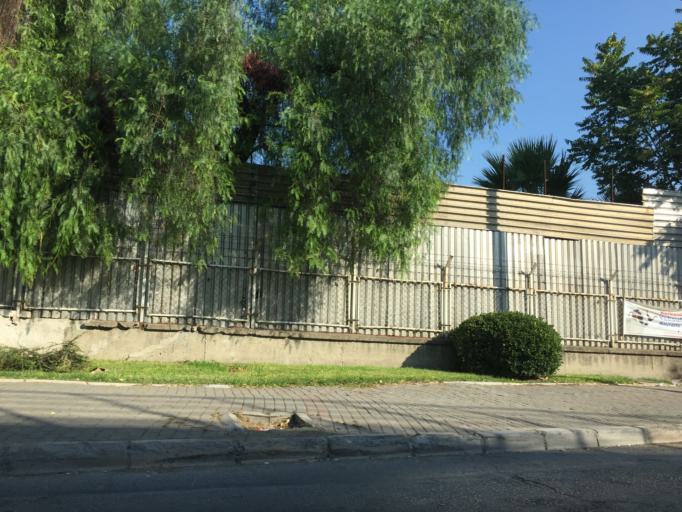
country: TR
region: Izmir
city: Buca
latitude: 38.4433
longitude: 27.1820
